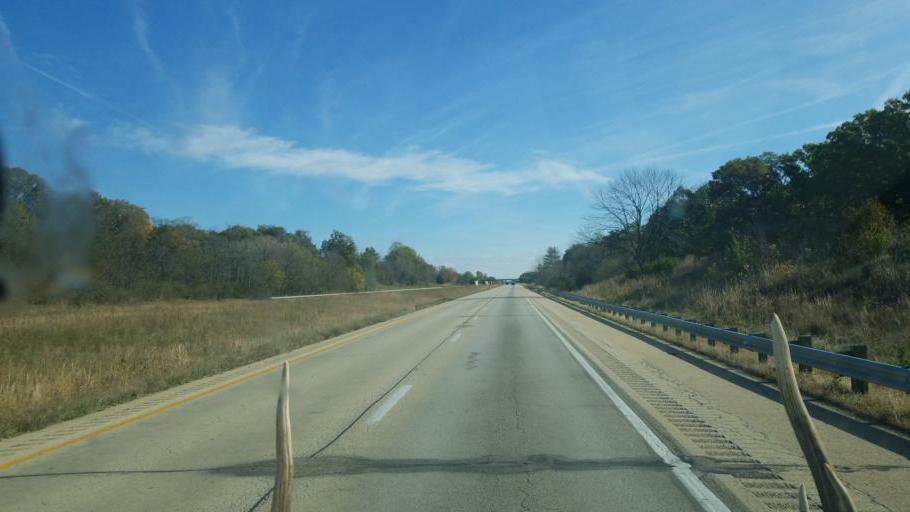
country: US
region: Illinois
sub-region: Effingham County
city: Effingham
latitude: 39.0816
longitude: -88.6252
